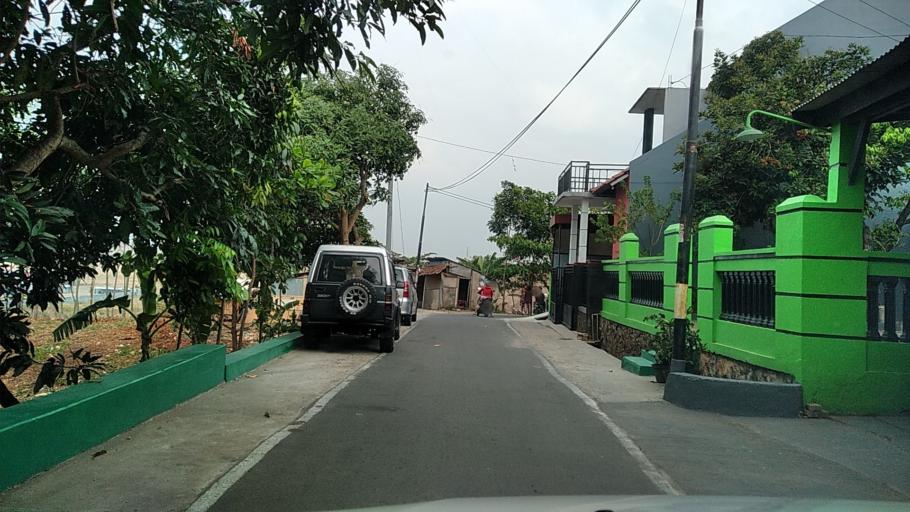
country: ID
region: Central Java
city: Semarang
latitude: -7.0179
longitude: 110.3394
